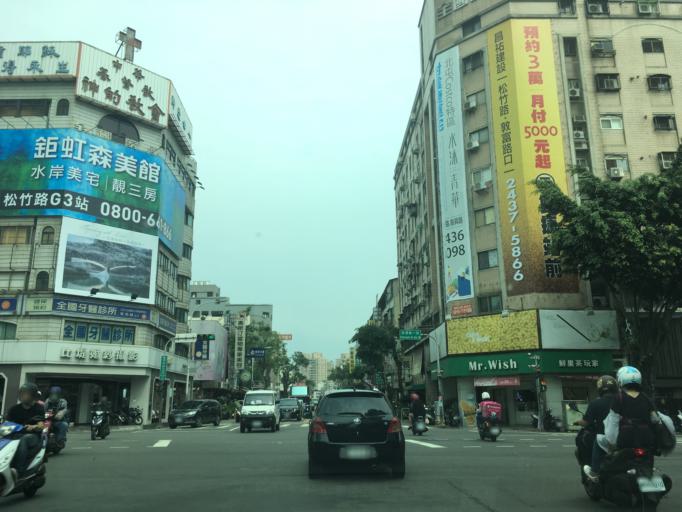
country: TW
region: Taiwan
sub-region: Taichung City
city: Taichung
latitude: 24.1670
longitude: 120.6848
